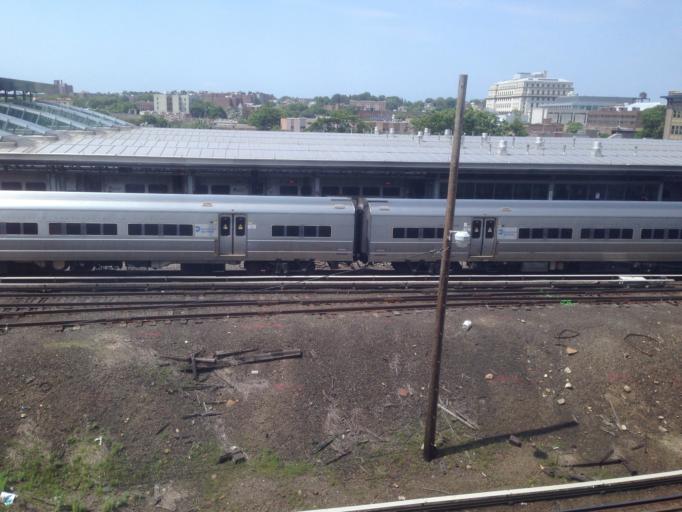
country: US
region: New York
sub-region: Queens County
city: Jamaica
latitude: 40.6991
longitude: -73.8090
